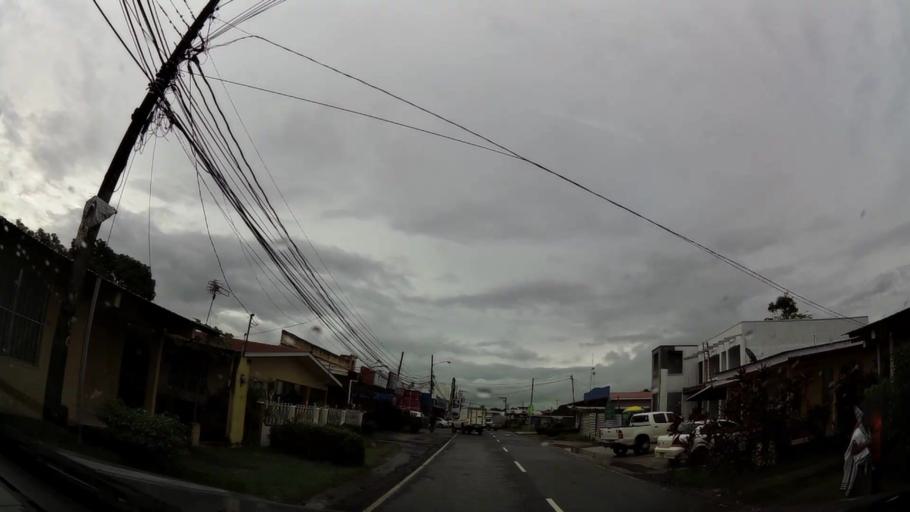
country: PA
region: Veraguas
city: Santiago de Veraguas
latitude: 8.0958
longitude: -80.9766
